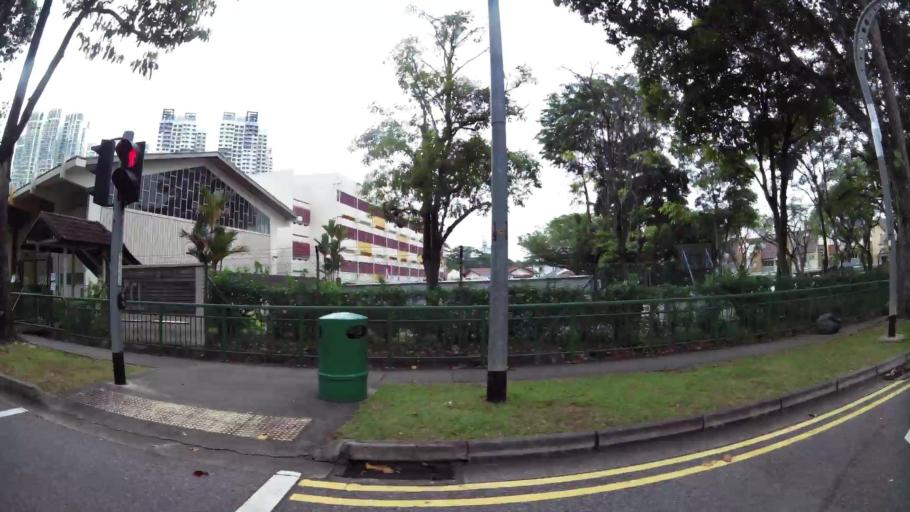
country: SG
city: Singapore
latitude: 1.3122
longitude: 103.7860
